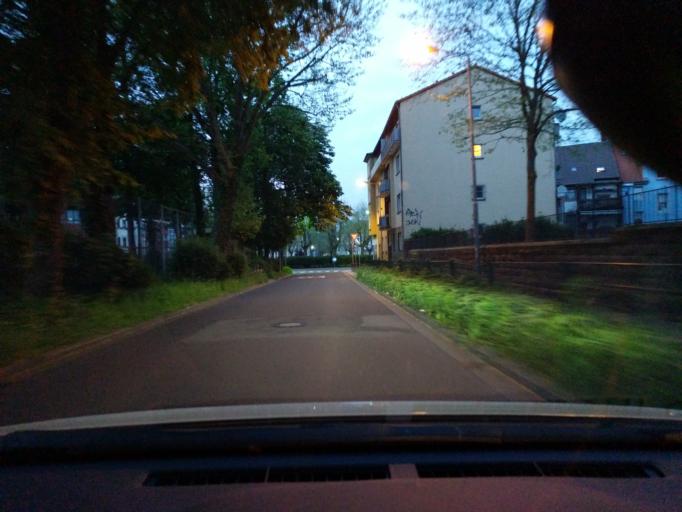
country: DE
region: Rheinland-Pfalz
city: Kaiserslautern
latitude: 49.4401
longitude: 7.7765
